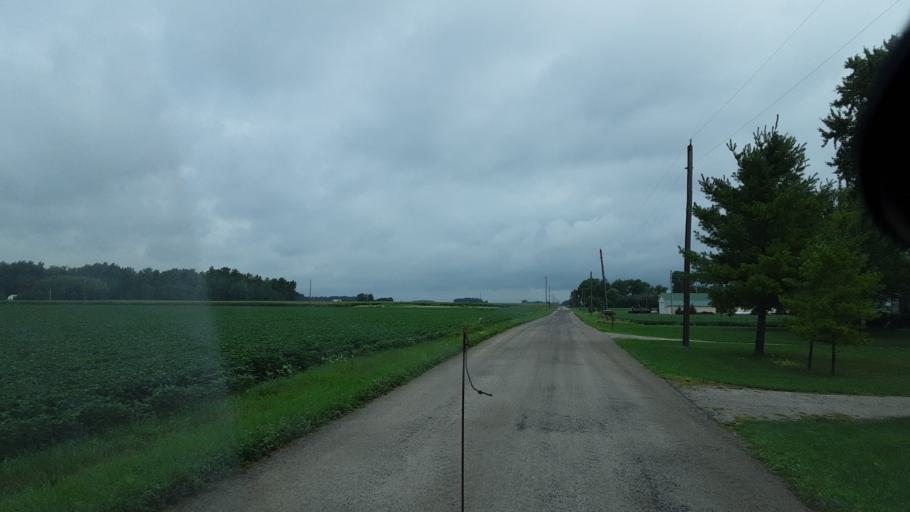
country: US
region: Indiana
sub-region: Allen County
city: Monroeville
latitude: 40.9039
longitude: -84.8425
